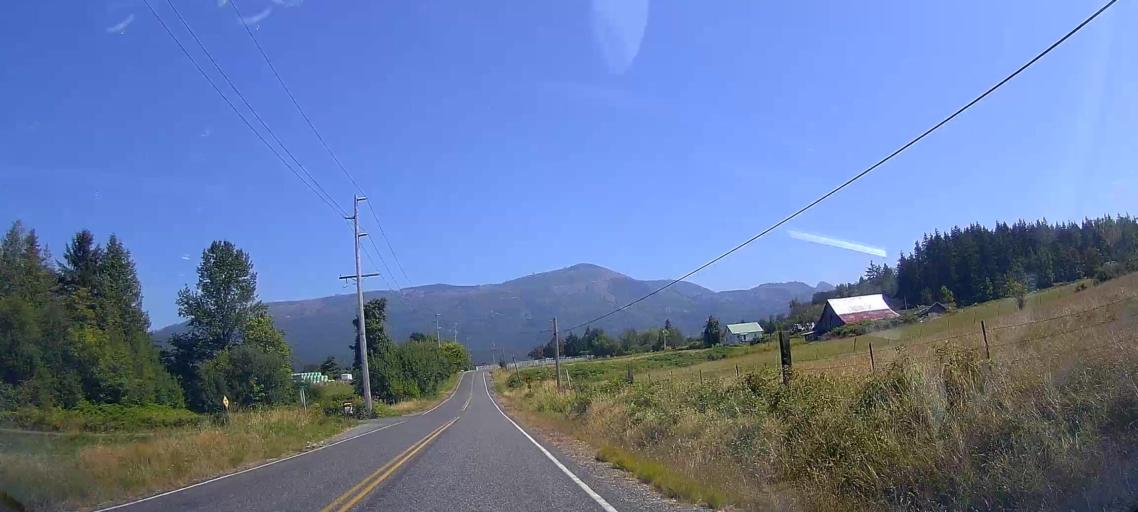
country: US
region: Washington
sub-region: Skagit County
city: Clear Lake
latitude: 48.4354
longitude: -122.2452
